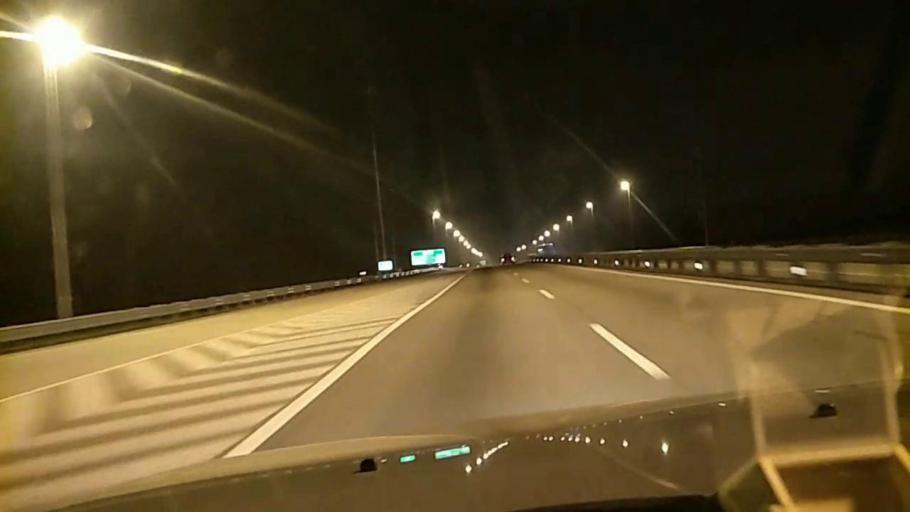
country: MY
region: Penang
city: Juru
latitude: 5.2521
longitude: 100.4692
